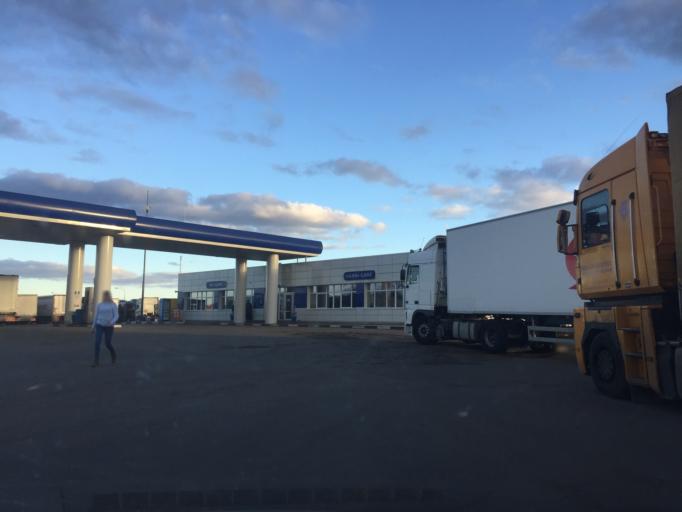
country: BY
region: Vitebsk
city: Myory
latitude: 55.8149
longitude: 27.6697
